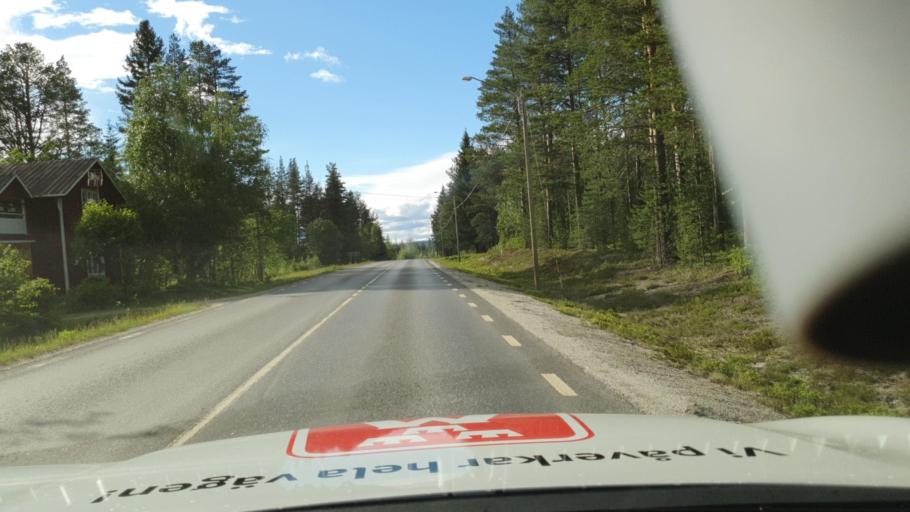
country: SE
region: Vaesterbotten
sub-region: Lycksele Kommun
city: Soderfors
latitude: 64.7911
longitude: 18.1070
